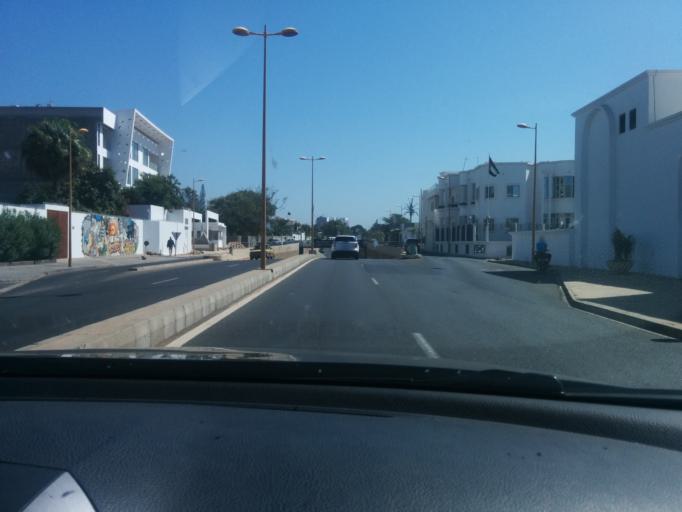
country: SN
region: Dakar
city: Mermoz Boabab
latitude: 14.7016
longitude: -17.4767
